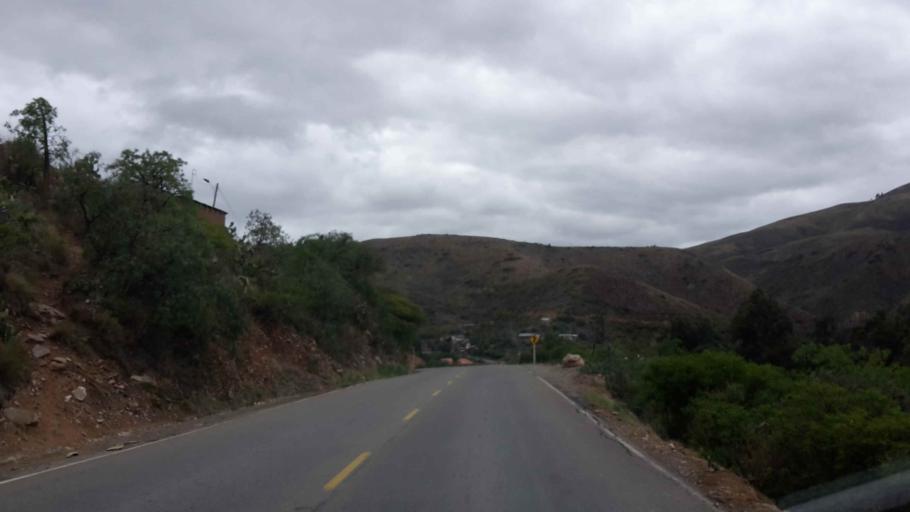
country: BO
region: Cochabamba
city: Punata
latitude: -17.5083
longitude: -65.8046
